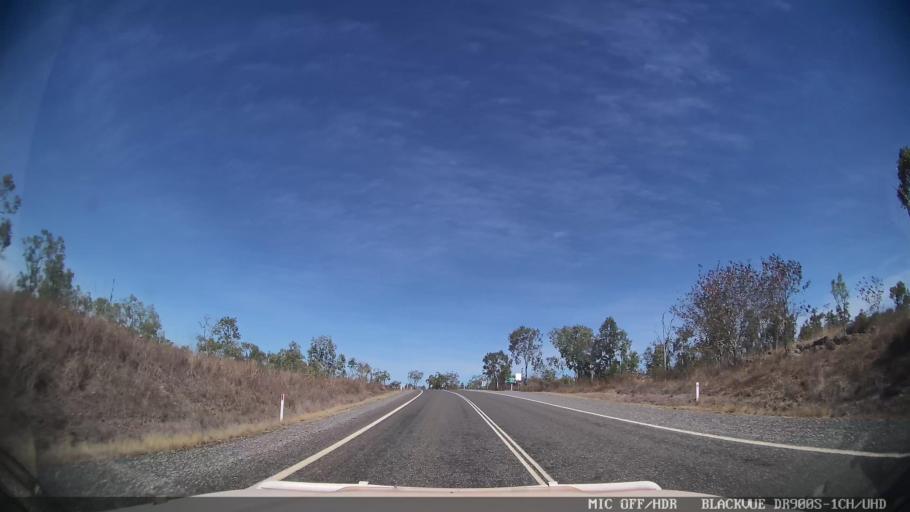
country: AU
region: Queensland
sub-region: Cook
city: Cooktown
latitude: -15.8629
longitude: 144.8030
